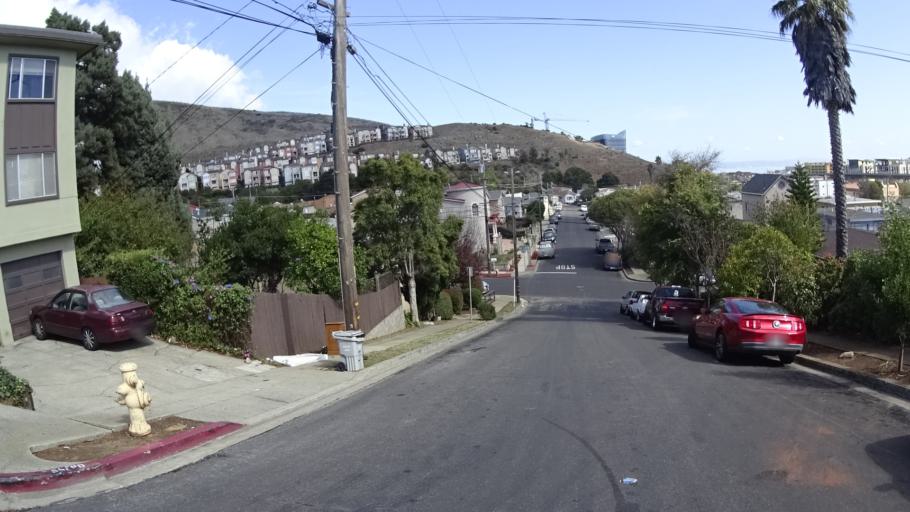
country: US
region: California
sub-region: San Mateo County
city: South San Francisco
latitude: 37.6634
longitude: -122.4036
